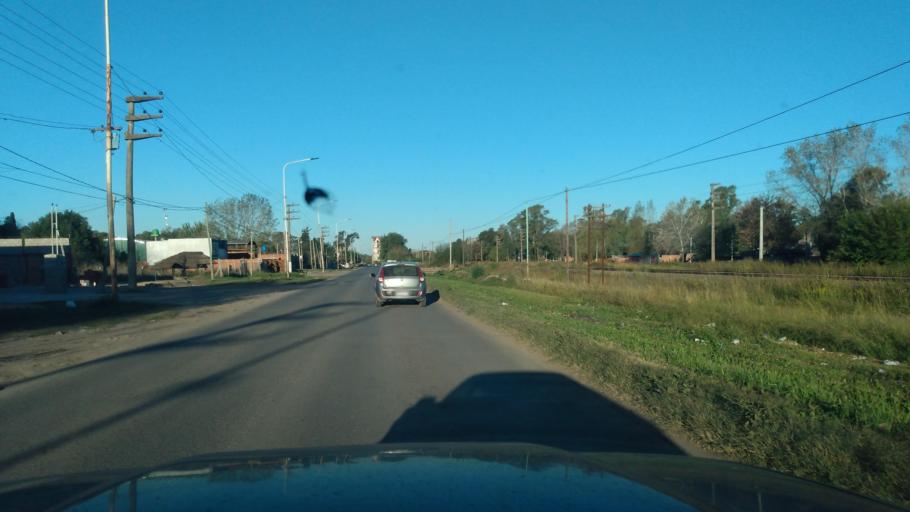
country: AR
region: Buenos Aires
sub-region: Partido de General Rodriguez
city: General Rodriguez
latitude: -34.6279
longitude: -58.8702
